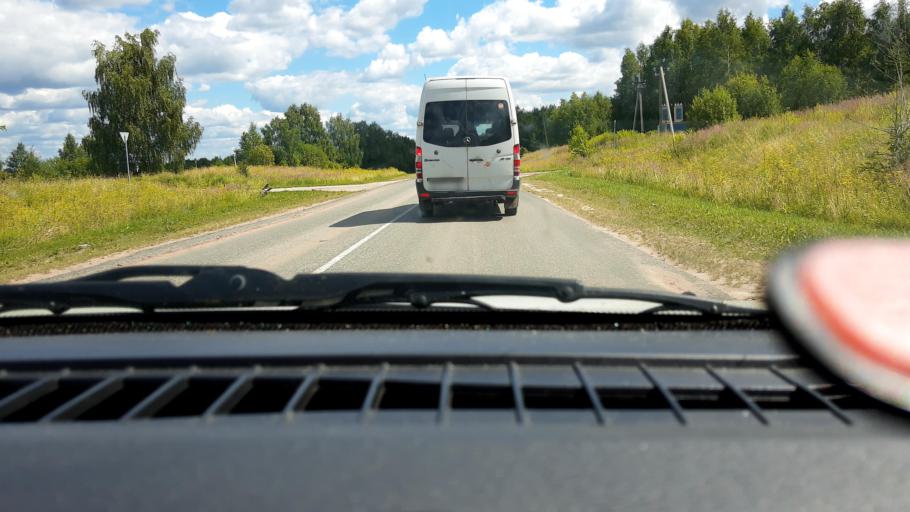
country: RU
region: Nizjnij Novgorod
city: Afonino
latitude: 56.1204
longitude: 43.9935
